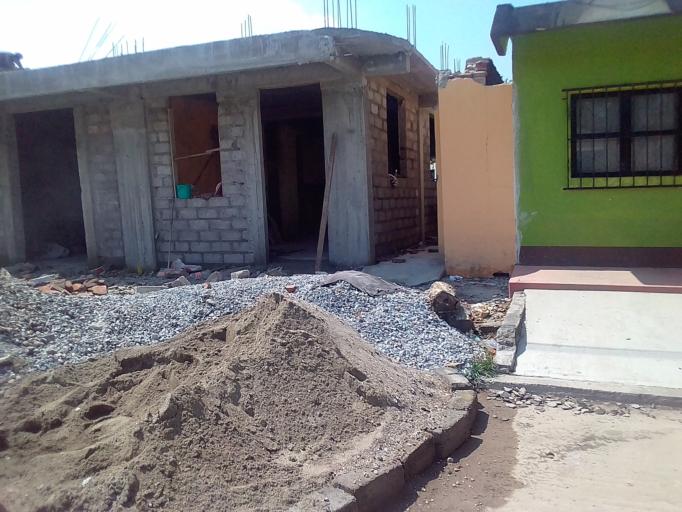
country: MX
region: Oaxaca
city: Union Hidalgo
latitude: 16.4744
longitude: -94.8290
